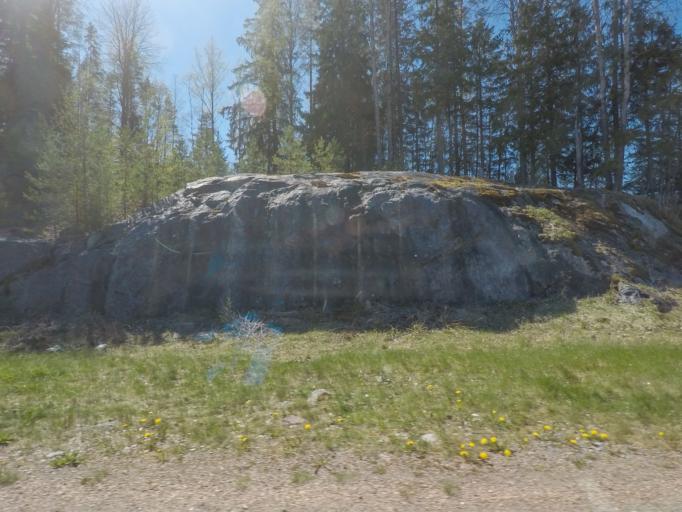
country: FI
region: Uusimaa
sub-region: Helsinki
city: Sammatti
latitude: 60.3770
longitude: 23.8064
